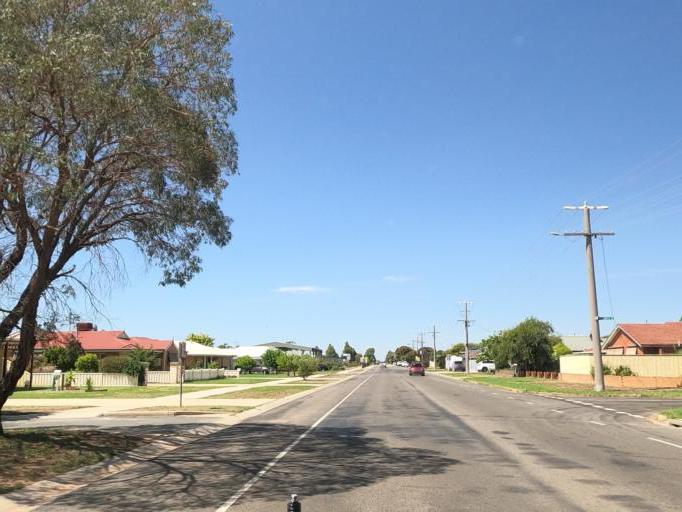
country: AU
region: Victoria
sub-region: Moira
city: Yarrawonga
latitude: -36.0098
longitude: 146.0132
